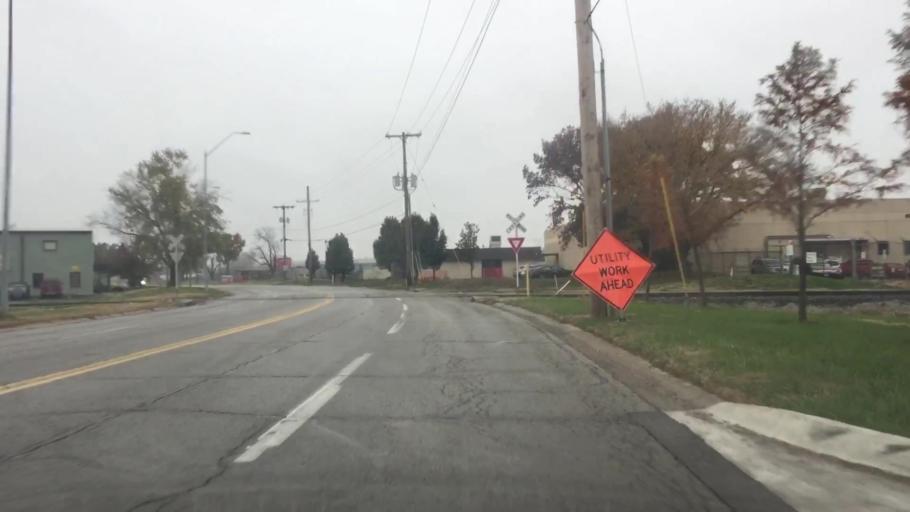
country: US
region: Missouri
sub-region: Clay County
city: North Kansas City
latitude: 39.1429
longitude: -94.5190
